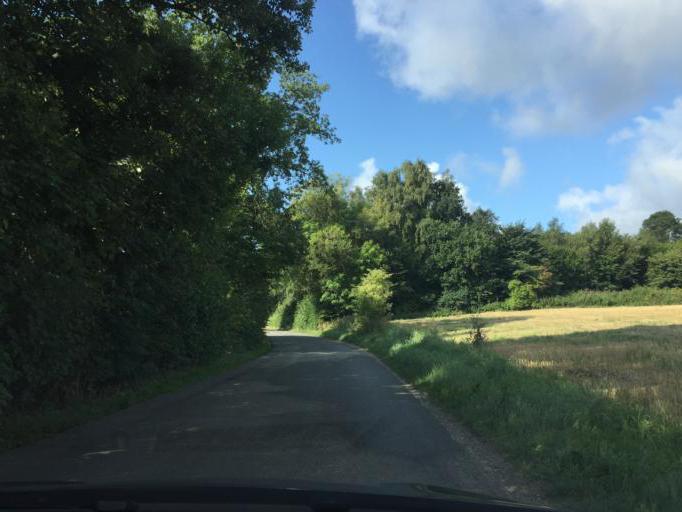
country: DK
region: South Denmark
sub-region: Faaborg-Midtfyn Kommune
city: Faaborg
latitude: 55.2020
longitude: 10.2882
